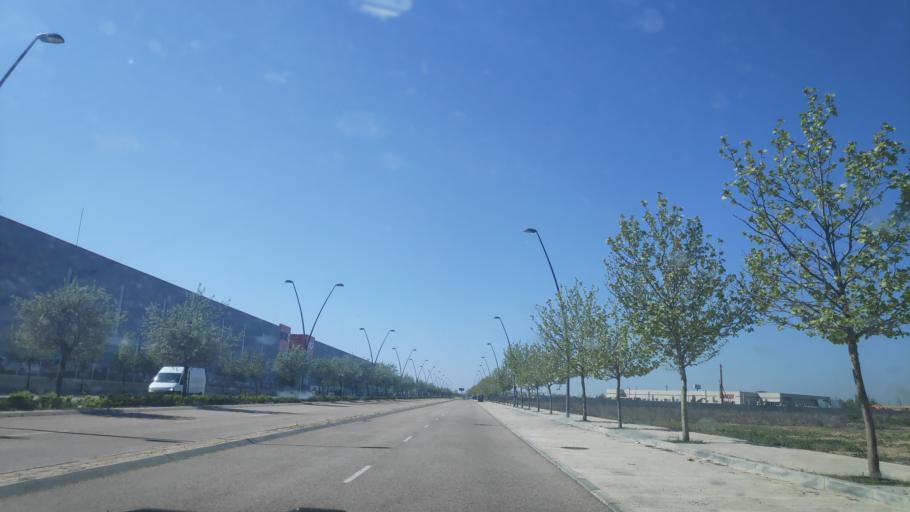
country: ES
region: Madrid
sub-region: Provincia de Madrid
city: Pinto
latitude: 40.2861
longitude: -3.6837
